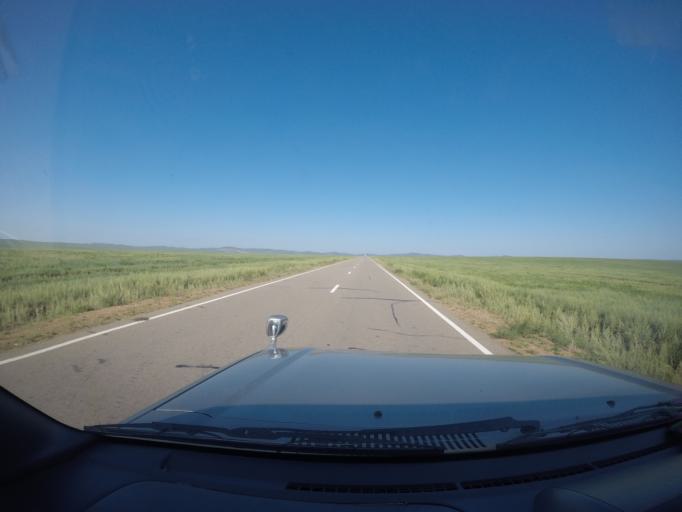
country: MN
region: Suhbaatar
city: Hanhohiy
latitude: 47.5698
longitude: 112.2518
